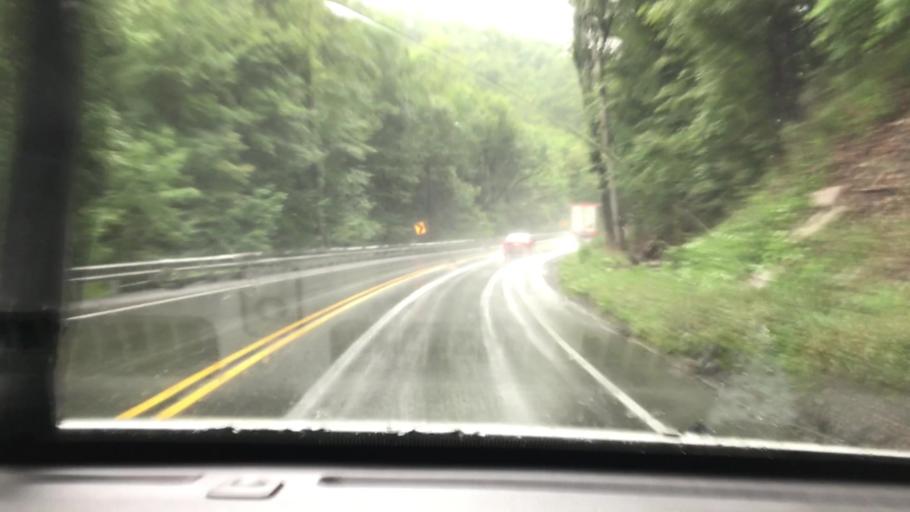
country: US
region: Pennsylvania
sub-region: Blair County
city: Tyrone
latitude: 40.7627
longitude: -78.2342
